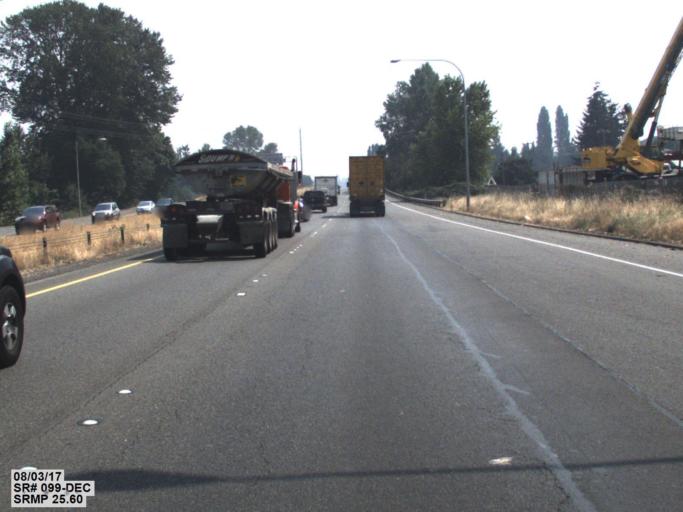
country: US
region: Washington
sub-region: King County
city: White Center
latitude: 47.5289
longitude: -122.3271
